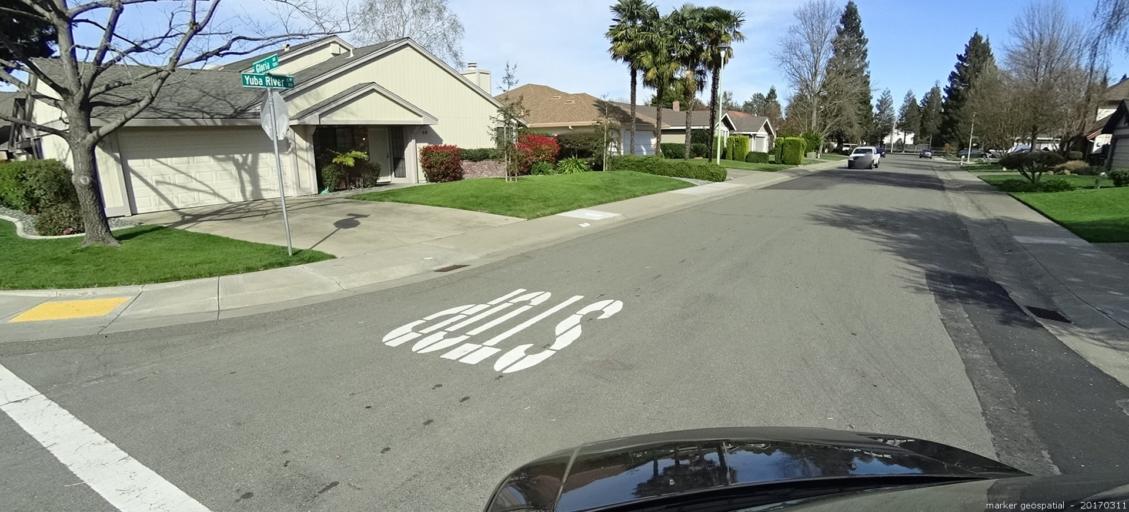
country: US
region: California
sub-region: Yolo County
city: West Sacramento
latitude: 38.4986
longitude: -121.5444
